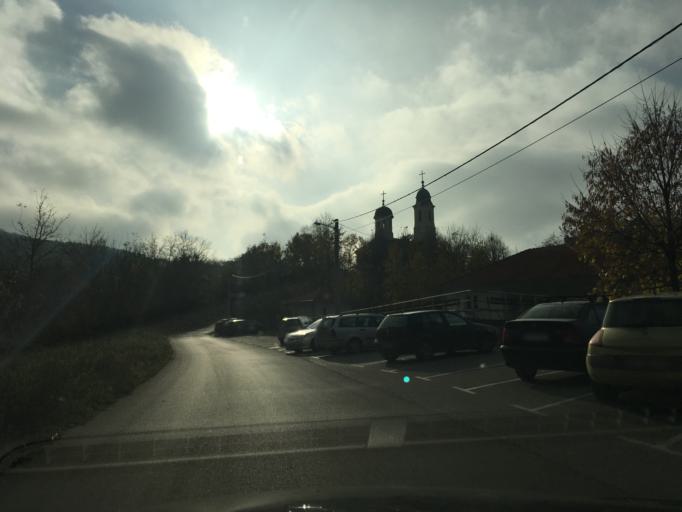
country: RS
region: Central Serbia
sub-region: Belgrade
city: Sopot
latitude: 44.4920
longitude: 20.5755
